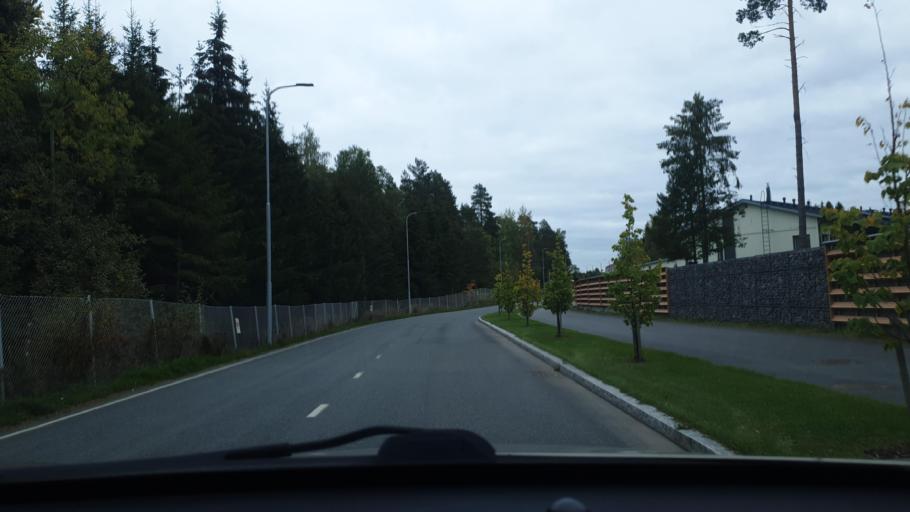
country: FI
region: Ostrobothnia
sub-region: Vaasa
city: Vaasa
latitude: 63.1198
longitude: 21.6254
